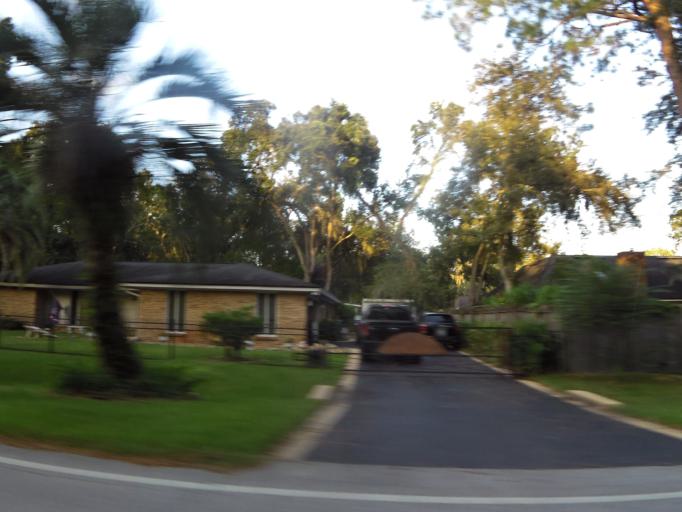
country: US
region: Florida
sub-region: Clay County
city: Orange Park
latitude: 30.2013
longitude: -81.6359
